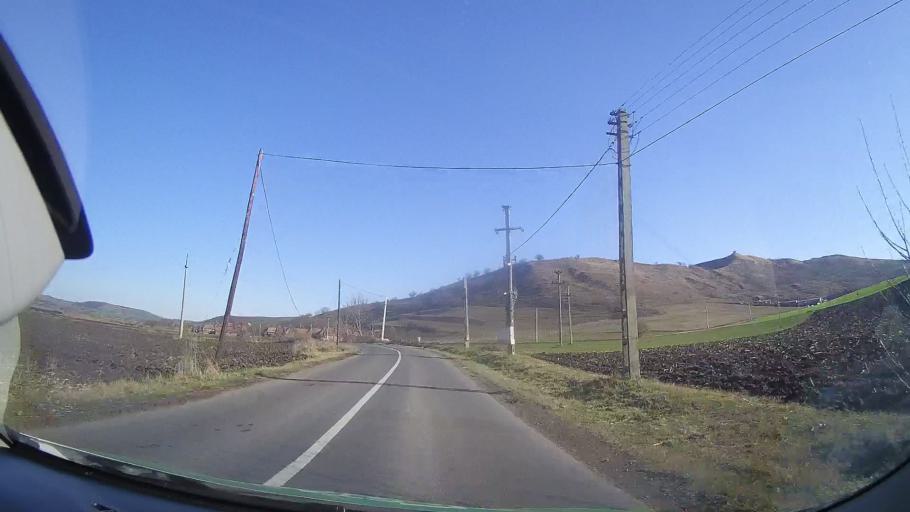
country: RO
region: Mures
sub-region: Comuna Band
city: Band
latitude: 46.5625
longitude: 24.3369
